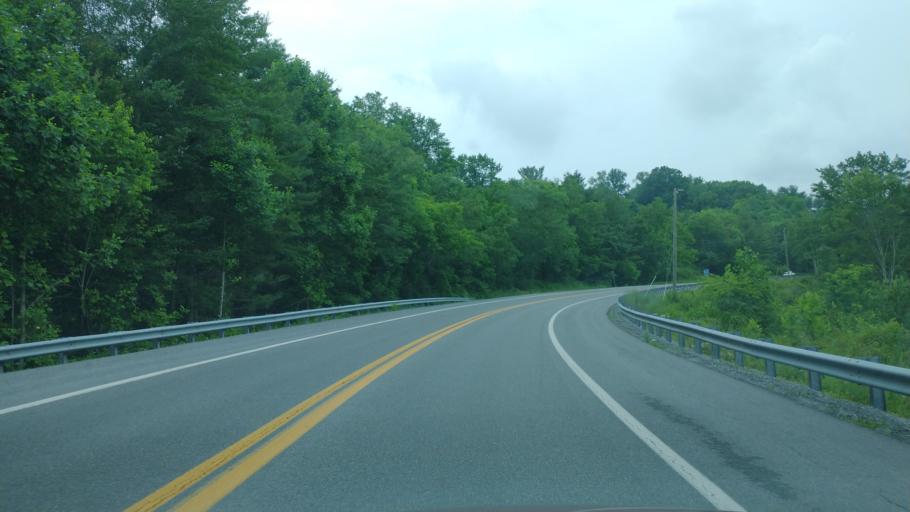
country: US
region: West Virginia
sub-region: Mercer County
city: Athens
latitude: 37.4181
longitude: -81.0598
